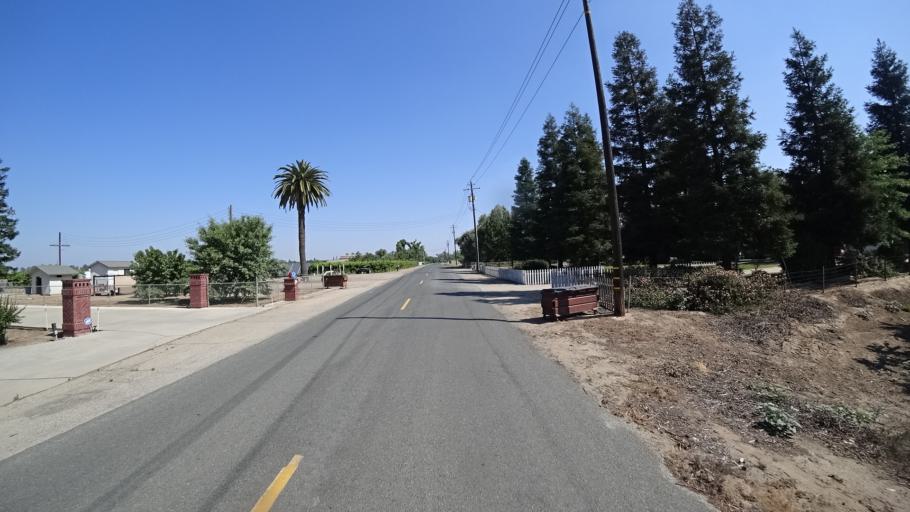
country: US
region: California
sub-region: Fresno County
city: Kingsburg
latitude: 36.4771
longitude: -119.5507
